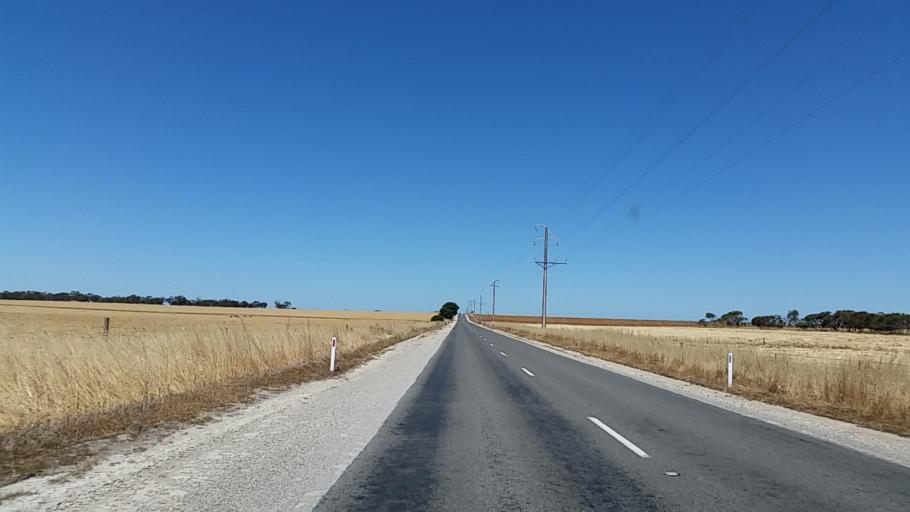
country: AU
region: South Australia
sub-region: Yorke Peninsula
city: Honiton
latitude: -35.0134
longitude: 137.6495
